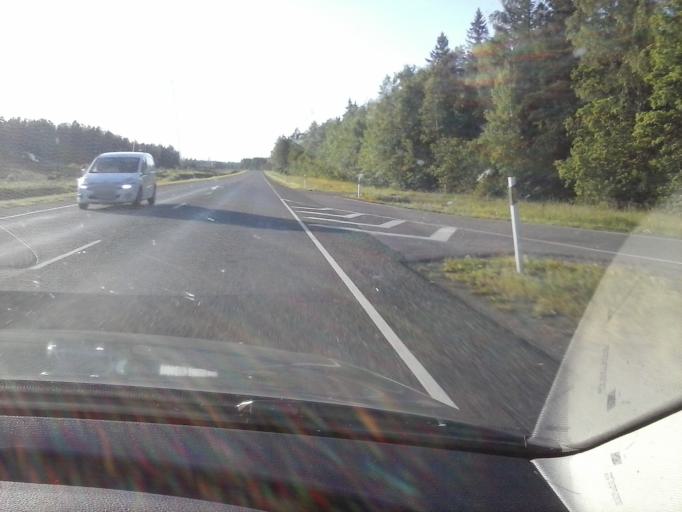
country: EE
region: Harju
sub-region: Nissi vald
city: Turba
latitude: 58.9662
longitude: 24.0686
